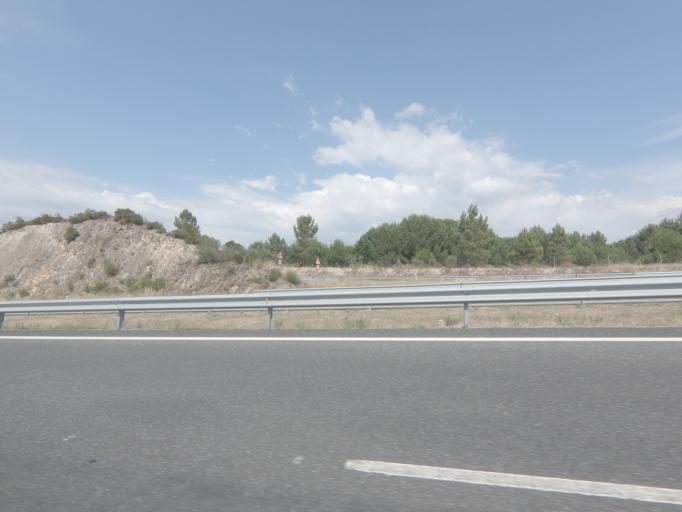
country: ES
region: Galicia
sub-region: Provincia de Ourense
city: Ourense
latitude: 42.3047
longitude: -7.8750
